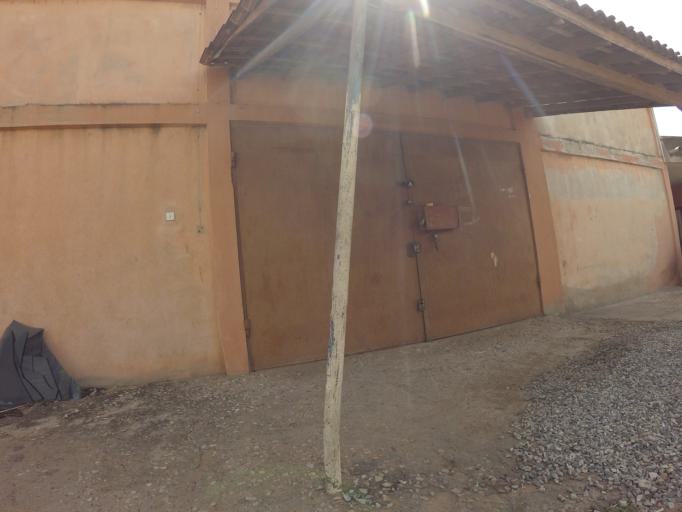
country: GH
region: Greater Accra
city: Dome
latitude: 5.6249
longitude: -0.2317
